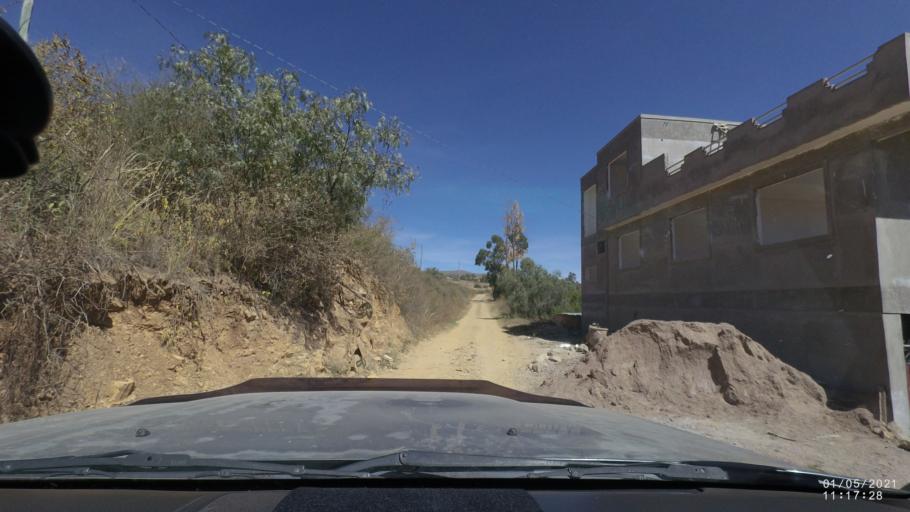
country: BO
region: Cochabamba
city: Tarata
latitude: -17.6395
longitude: -66.1139
